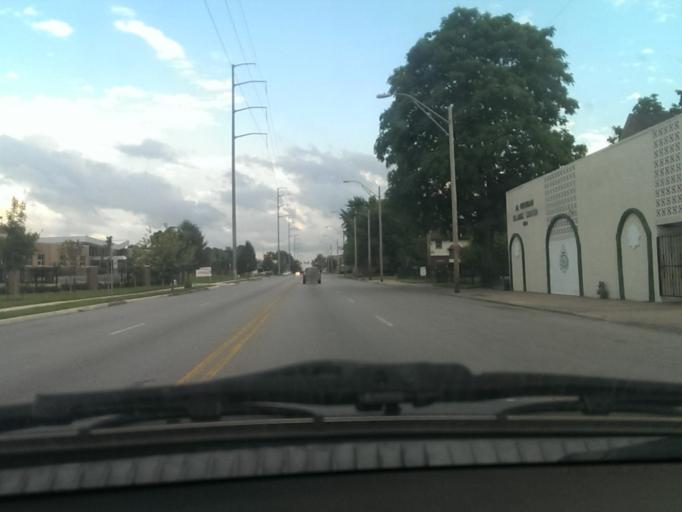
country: US
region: Missouri
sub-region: Jackson County
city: Kansas City
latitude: 39.0597
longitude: -94.5720
